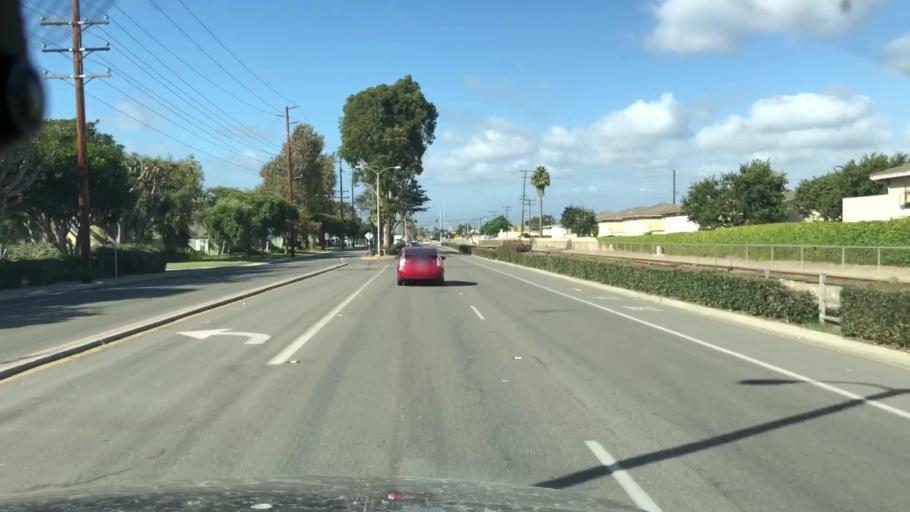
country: US
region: California
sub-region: Ventura County
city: Channel Islands Beach
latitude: 34.1792
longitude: -119.2083
